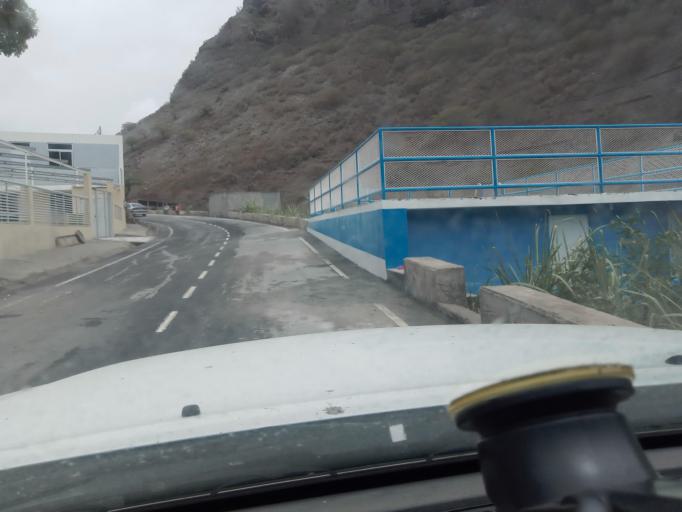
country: CV
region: Sao Miguel
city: Calheta
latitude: 15.1464
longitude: -23.6128
